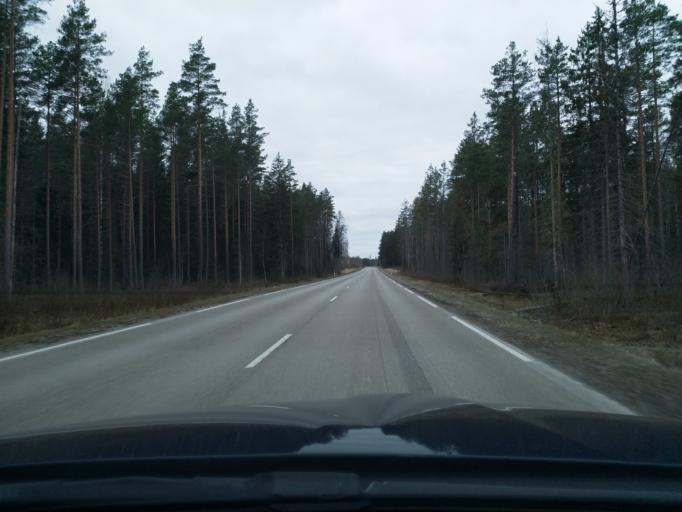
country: LV
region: Kuldigas Rajons
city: Kuldiga
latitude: 56.9513
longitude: 22.2551
